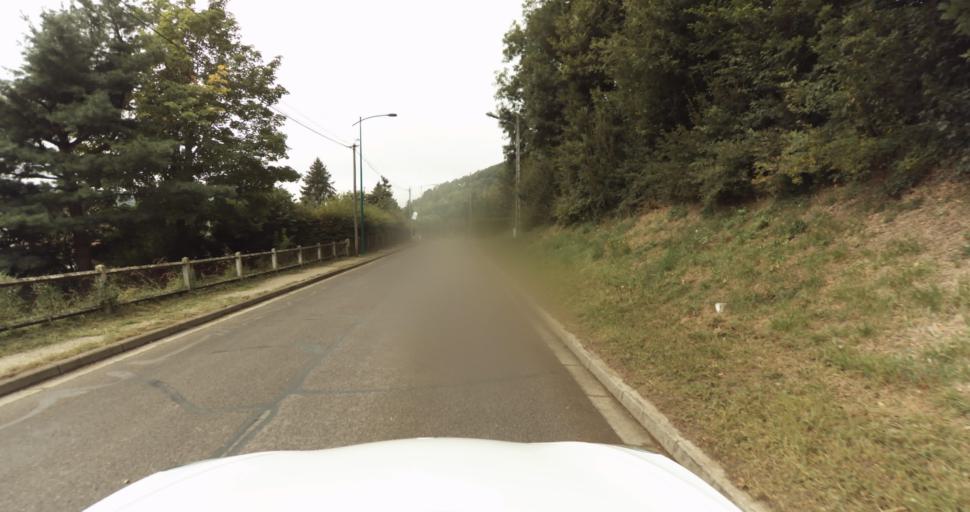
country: FR
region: Haute-Normandie
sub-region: Departement de l'Eure
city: Normanville
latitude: 49.0797
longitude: 1.1589
